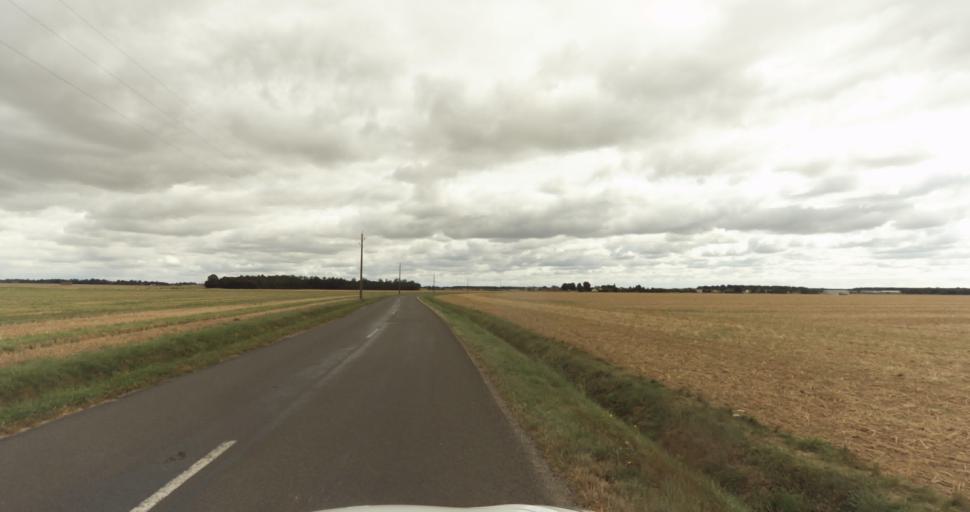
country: FR
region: Haute-Normandie
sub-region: Departement de l'Eure
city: Nonancourt
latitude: 48.8058
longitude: 1.1279
